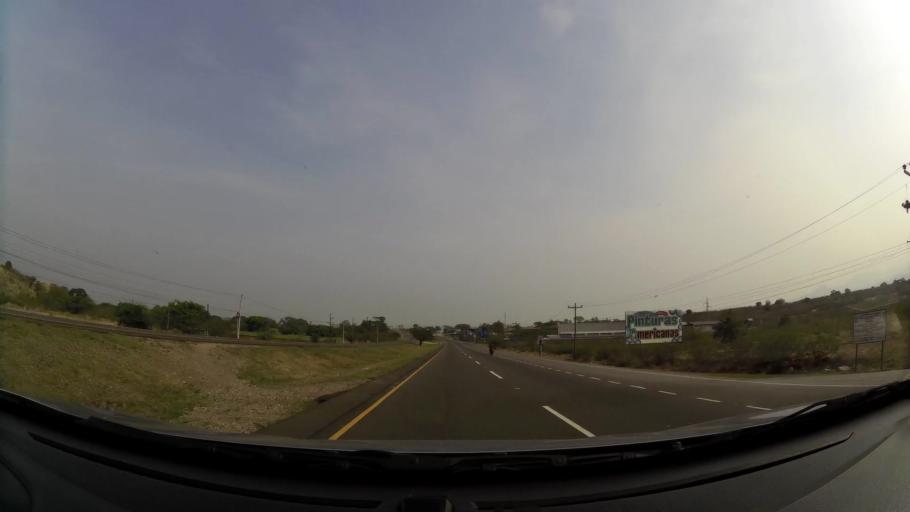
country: HN
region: Comayagua
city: Comayagua
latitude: 14.4143
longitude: -87.6240
